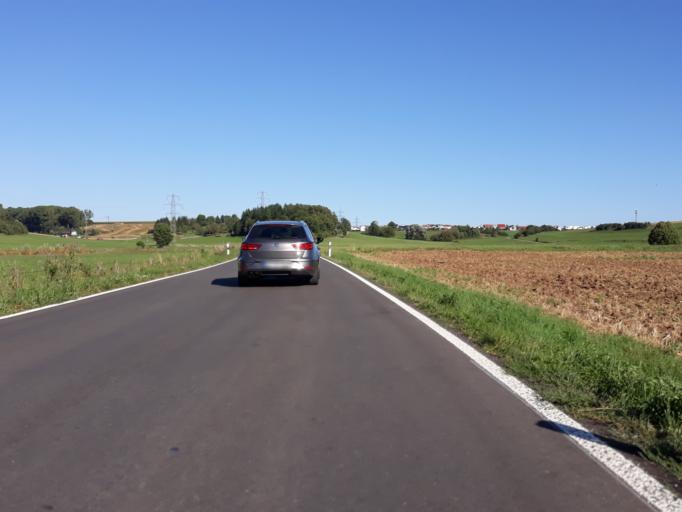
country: DE
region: Baden-Wuerttemberg
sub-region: Regierungsbezirk Stuttgart
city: Altdorf
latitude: 48.6472
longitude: 8.9874
